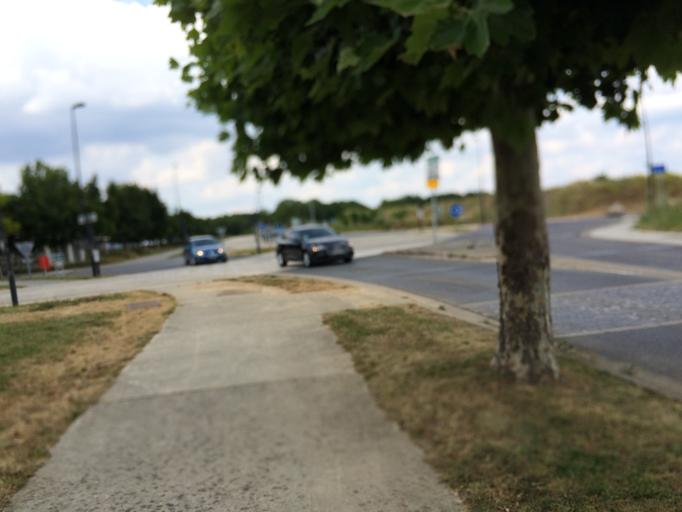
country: FR
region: Ile-de-France
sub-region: Departement de l'Essonne
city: Tigery
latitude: 48.6278
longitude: 2.5173
